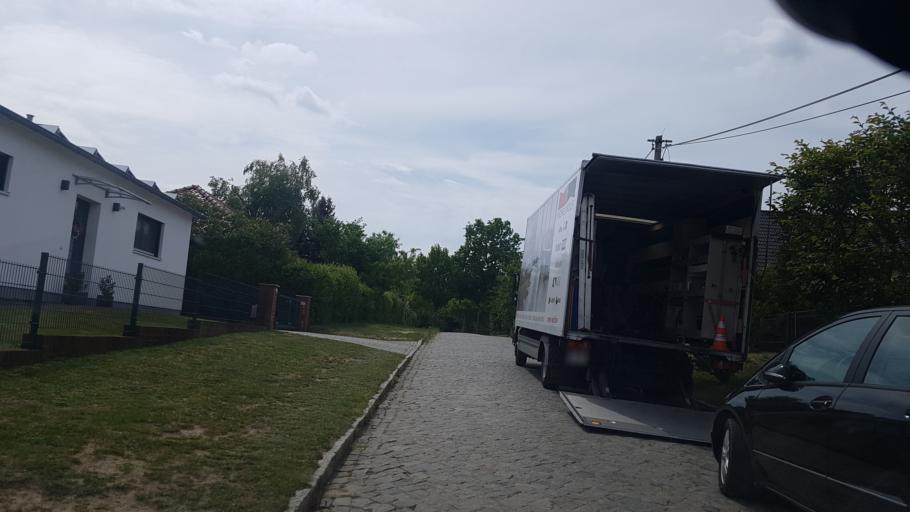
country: DE
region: Brandenburg
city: Michendorf
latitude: 52.3120
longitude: 13.0710
